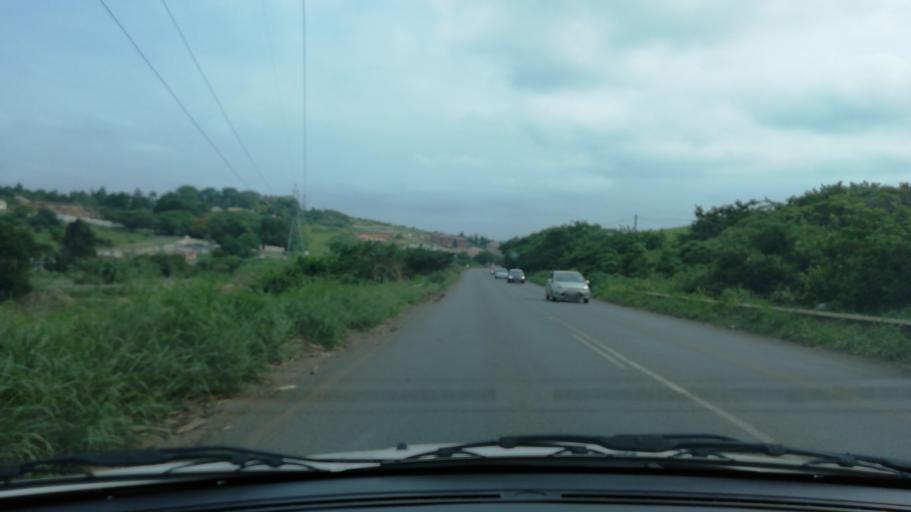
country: ZA
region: KwaZulu-Natal
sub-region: uThungulu District Municipality
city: Empangeni
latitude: -28.7457
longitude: 31.8807
